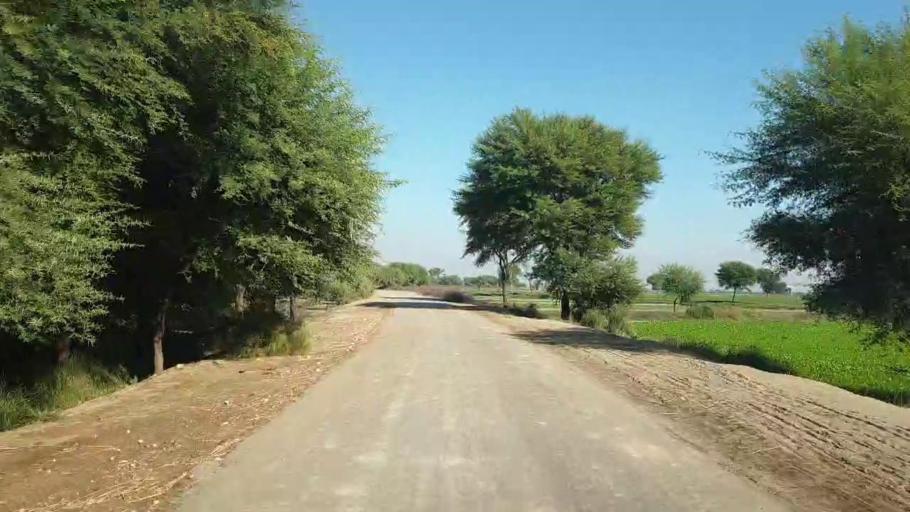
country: PK
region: Sindh
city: Dadu
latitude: 26.7930
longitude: 67.8262
